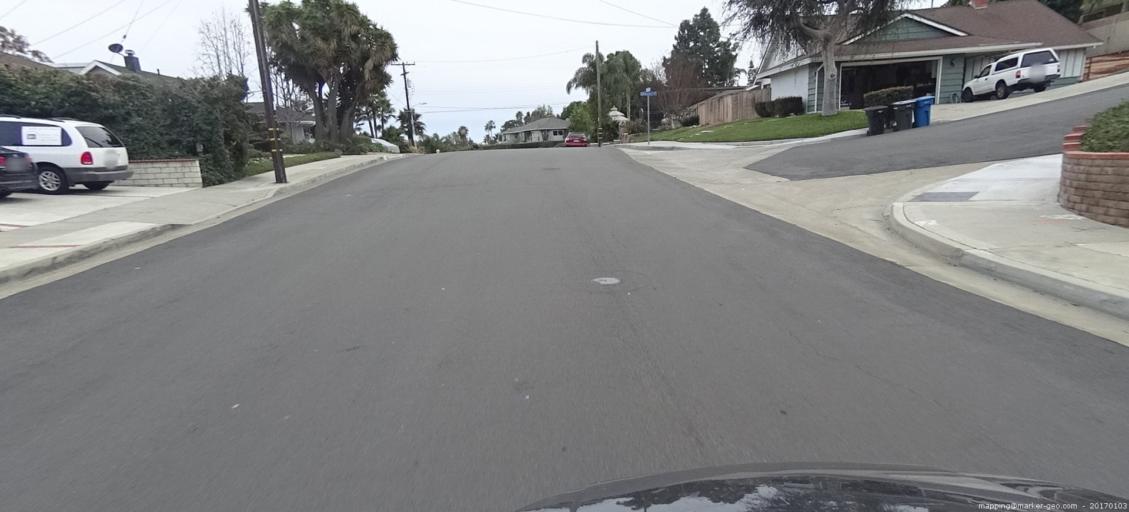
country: US
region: California
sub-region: Orange County
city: Dana Point
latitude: 33.4853
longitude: -117.6881
